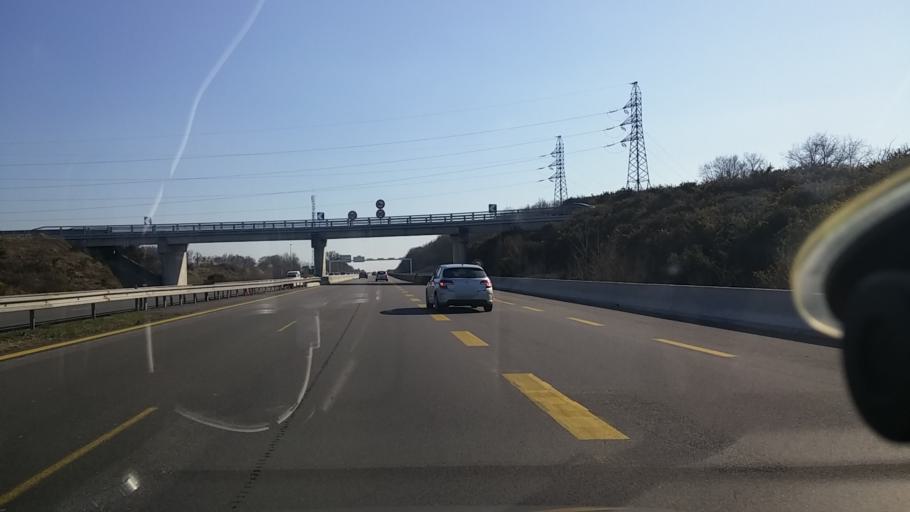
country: FR
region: Centre
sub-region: Departement du Loir-et-Cher
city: Theillay
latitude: 47.2868
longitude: 2.0435
